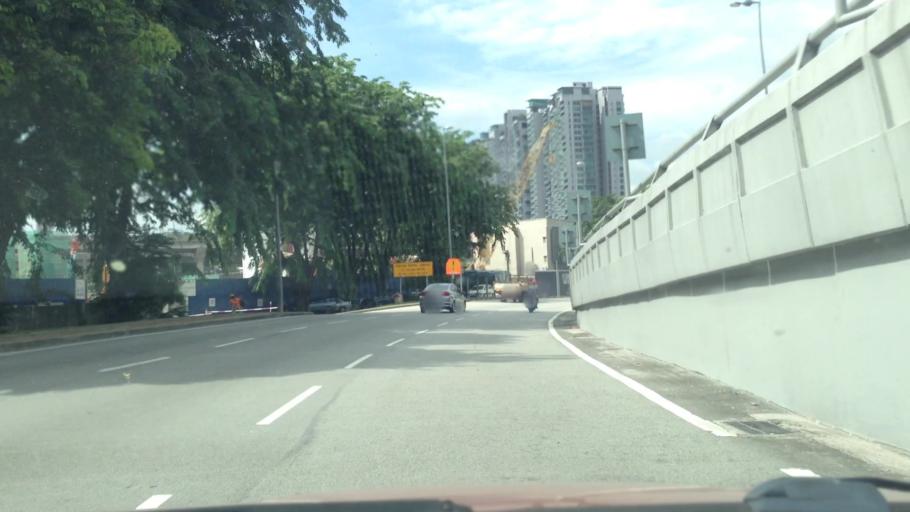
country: MY
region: Kuala Lumpur
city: Kuala Lumpur
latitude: 3.0899
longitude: 101.6927
